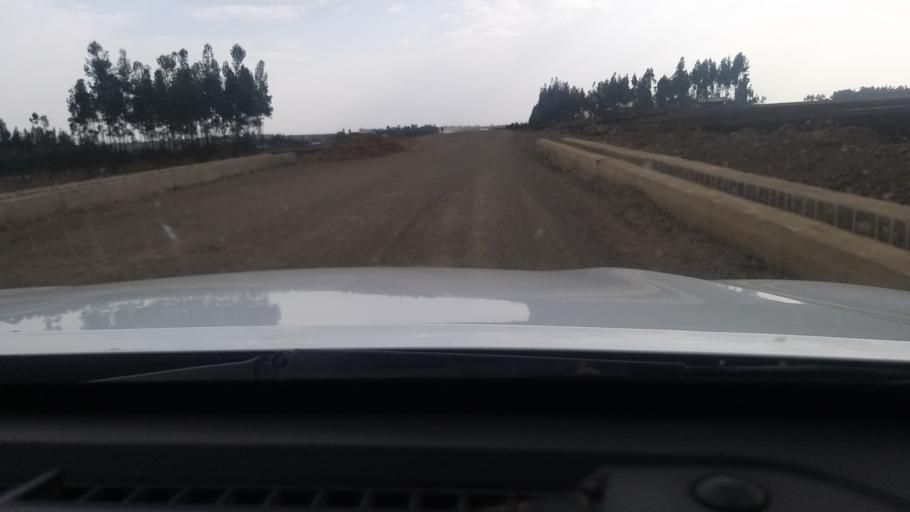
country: ET
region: Amhara
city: Were Ilu
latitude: 10.4533
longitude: 39.2108
